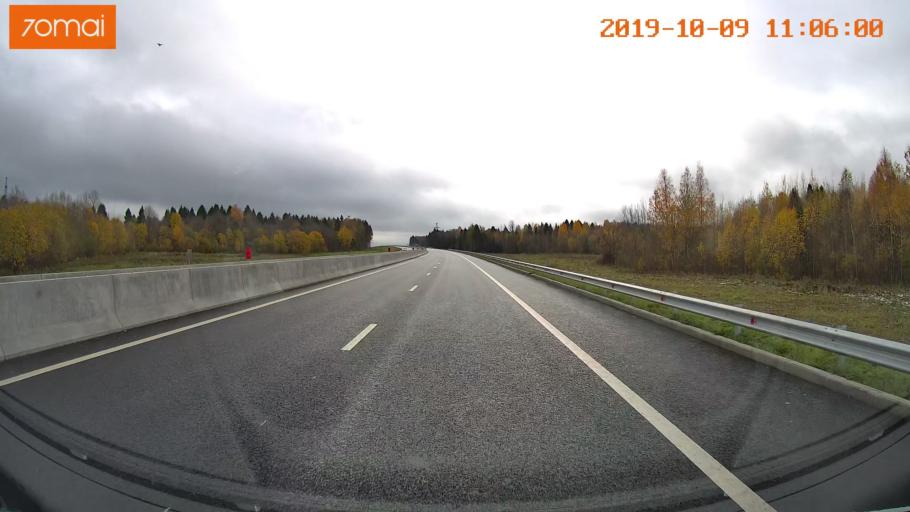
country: RU
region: Vologda
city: Molochnoye
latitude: 59.1922
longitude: 39.7582
